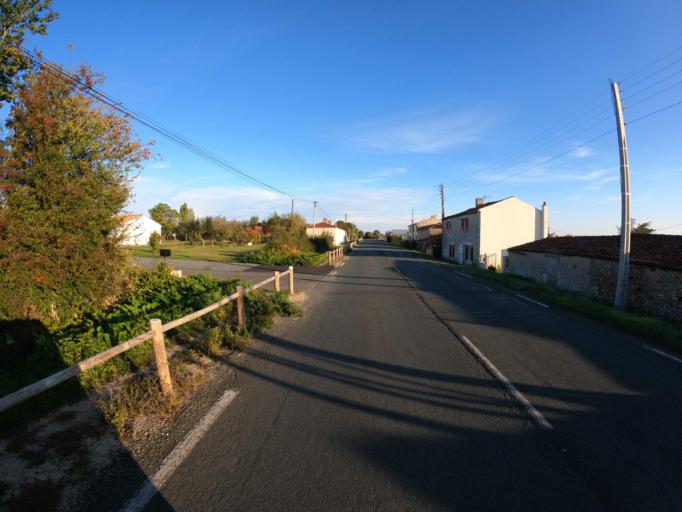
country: FR
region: Pays de la Loire
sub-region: Departement de la Vendee
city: Sainte-Hermine
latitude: 46.5518
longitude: -1.0451
